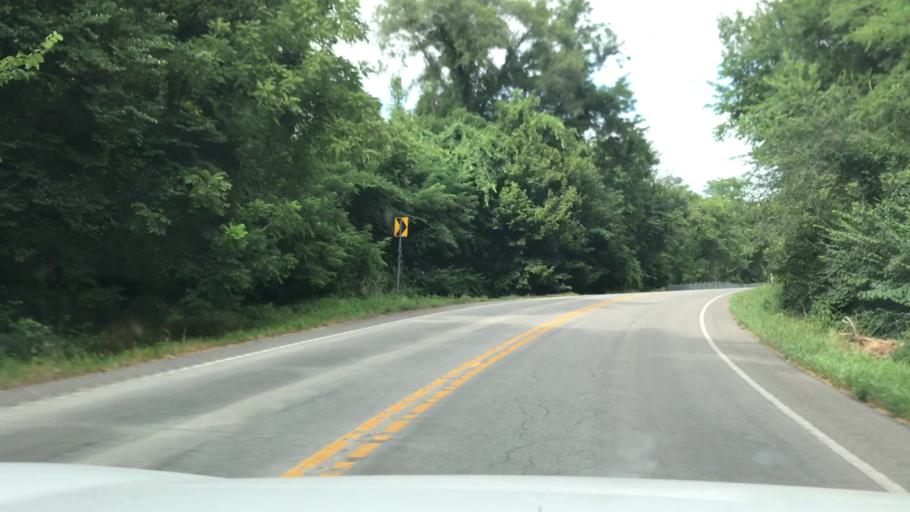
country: US
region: Missouri
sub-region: Saint Charles County
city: Weldon Spring
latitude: 38.6642
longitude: -90.7402
